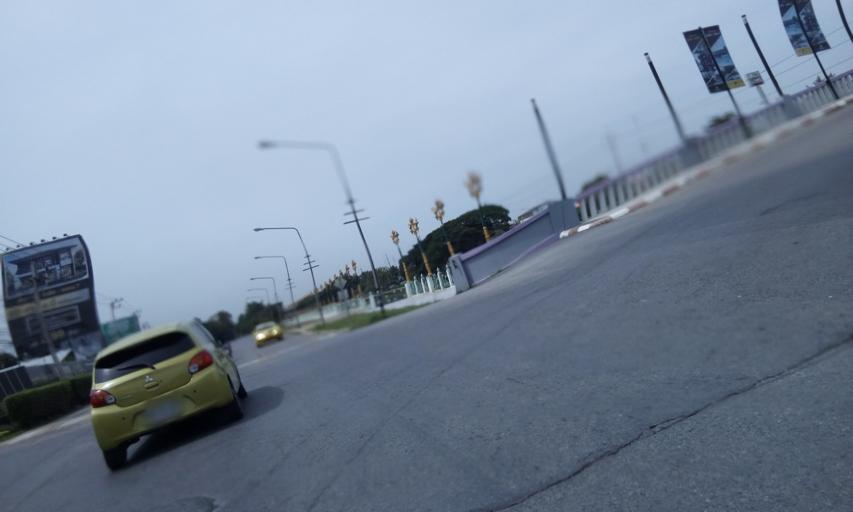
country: TH
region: Pathum Thani
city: Ban Rangsit
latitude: 14.0309
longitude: 100.7628
